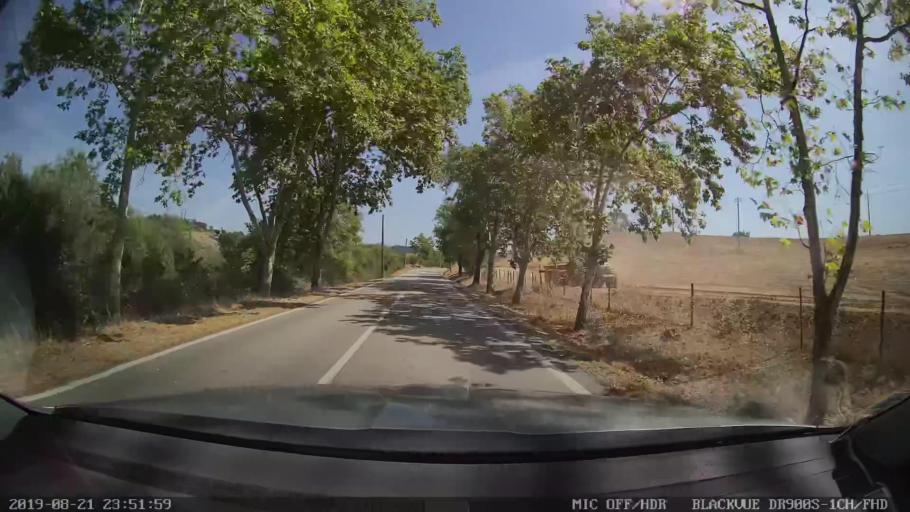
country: PT
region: Castelo Branco
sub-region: Idanha-A-Nova
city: Idanha-a-Nova
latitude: 39.9076
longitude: -7.2306
